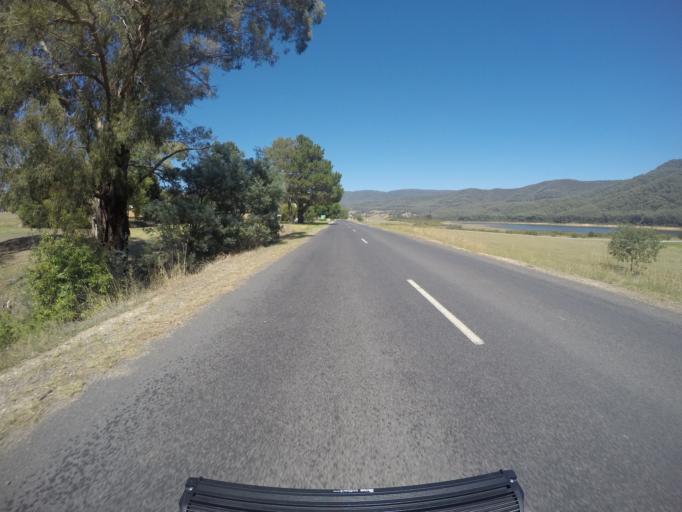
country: AU
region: New South Wales
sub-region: Tumut Shire
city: Tumut
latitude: -35.5804
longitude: 148.2979
